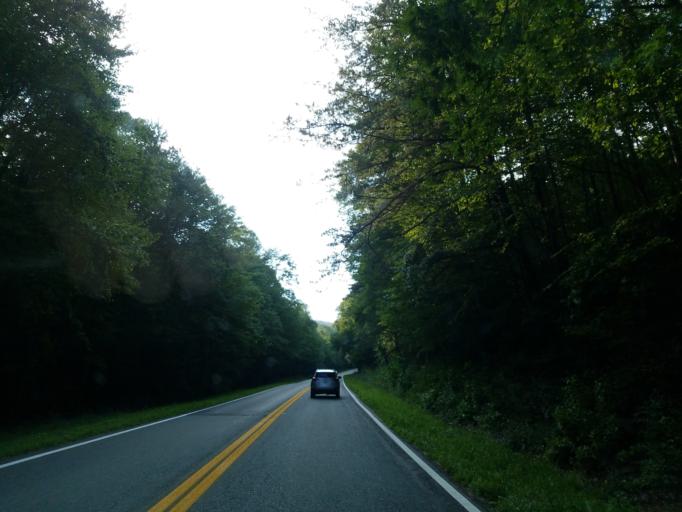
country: US
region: Georgia
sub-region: Fannin County
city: Blue Ridge
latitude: 34.8145
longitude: -84.2949
